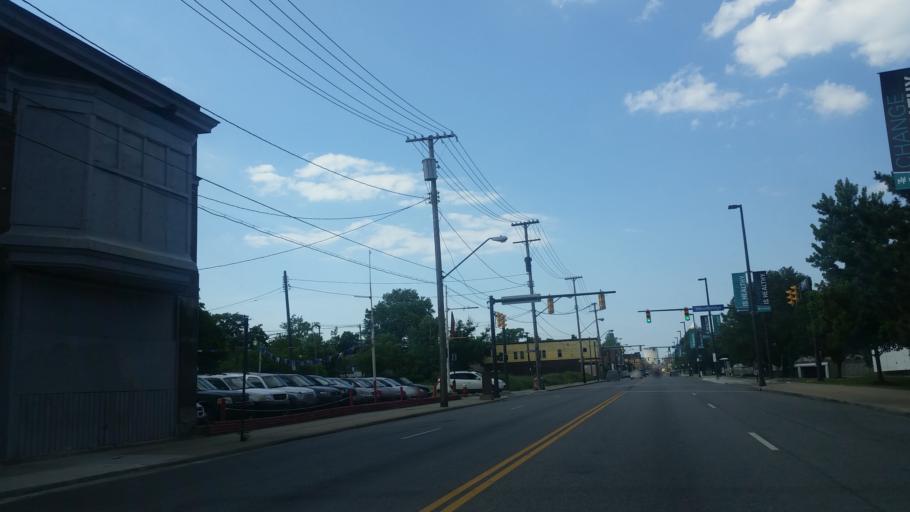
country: US
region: Ohio
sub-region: Cuyahoga County
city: Brooklyn Heights
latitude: 41.4604
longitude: -81.7007
